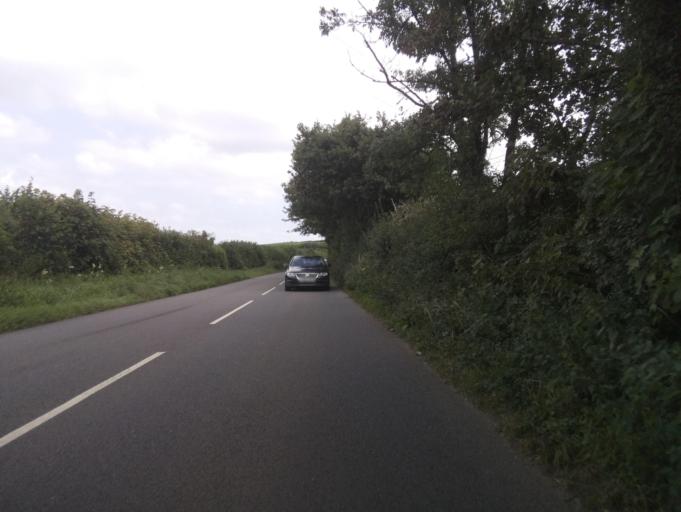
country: GB
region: England
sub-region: Devon
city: South Brent
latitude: 50.4222
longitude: -3.7763
